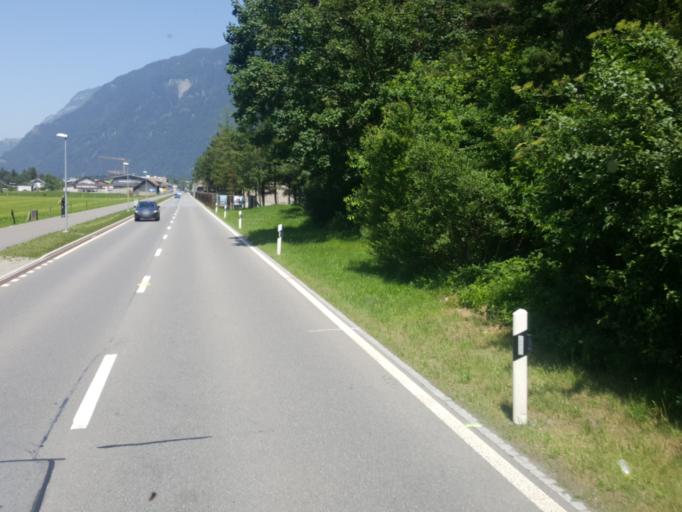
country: CH
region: Uri
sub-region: Uri
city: Schattdorf
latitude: 46.8461
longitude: 8.6457
